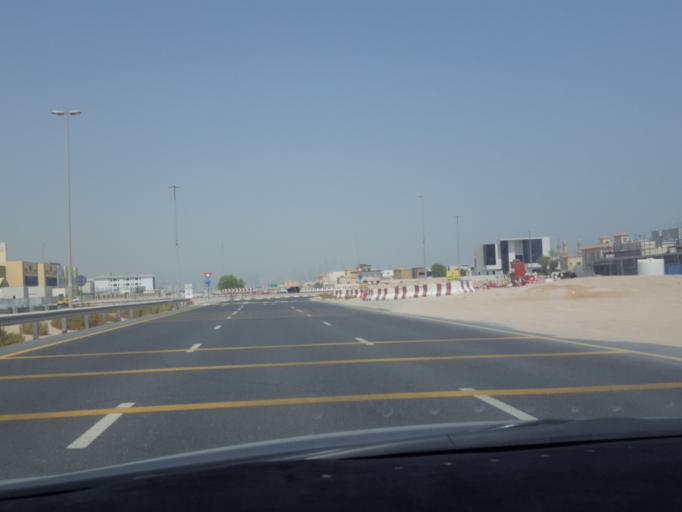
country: AE
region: Dubai
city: Dubai
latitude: 25.0808
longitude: 55.2330
